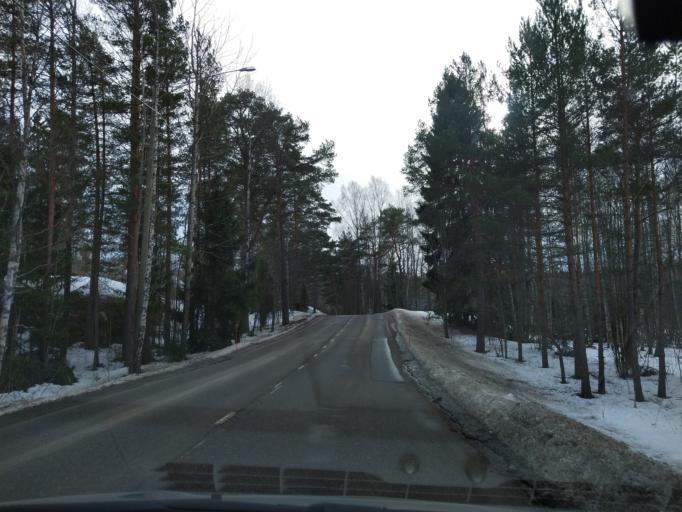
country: FI
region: Uusimaa
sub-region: Helsinki
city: Sibbo
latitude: 60.2683
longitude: 25.2861
